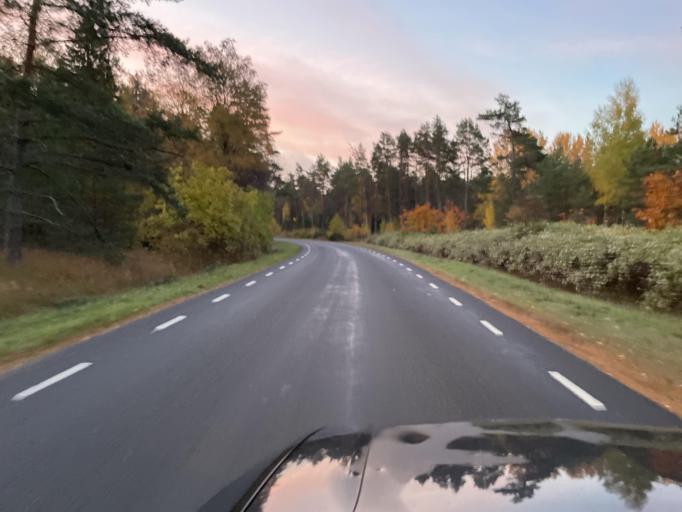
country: EE
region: Harju
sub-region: Nissi vald
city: Riisipere
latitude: 59.2524
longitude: 24.2317
